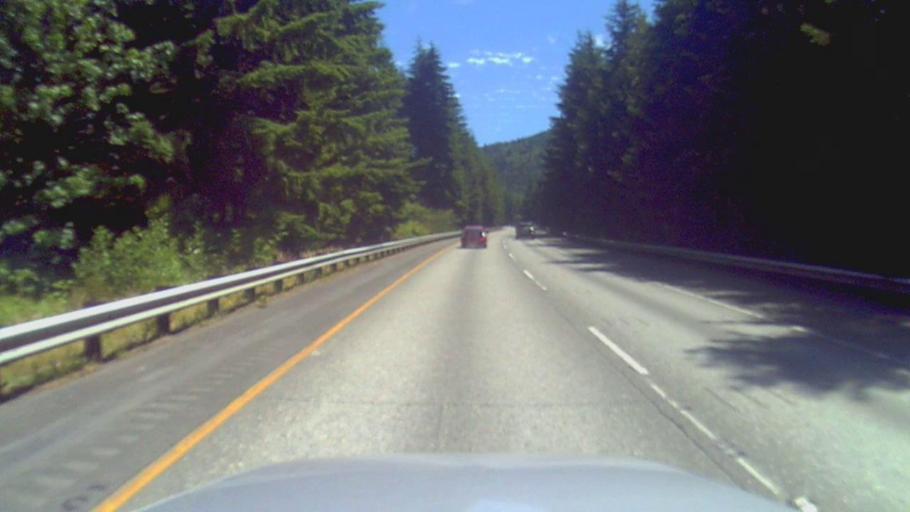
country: US
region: Washington
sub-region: Whatcom County
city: Geneva
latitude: 48.6900
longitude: -122.4287
